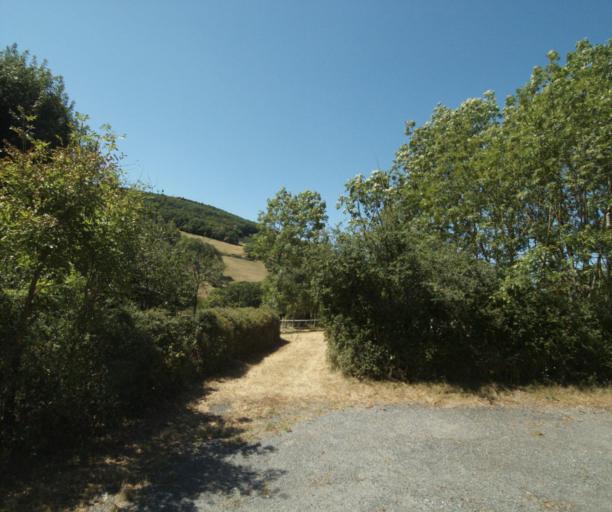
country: FR
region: Rhone-Alpes
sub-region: Departement du Rhone
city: Bessenay
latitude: 45.7914
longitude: 4.5263
